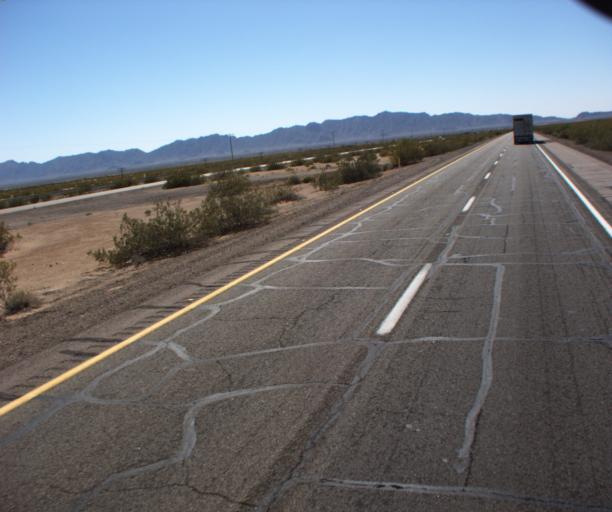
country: US
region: Arizona
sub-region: Yuma County
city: Wellton
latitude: 32.7663
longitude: -113.6214
